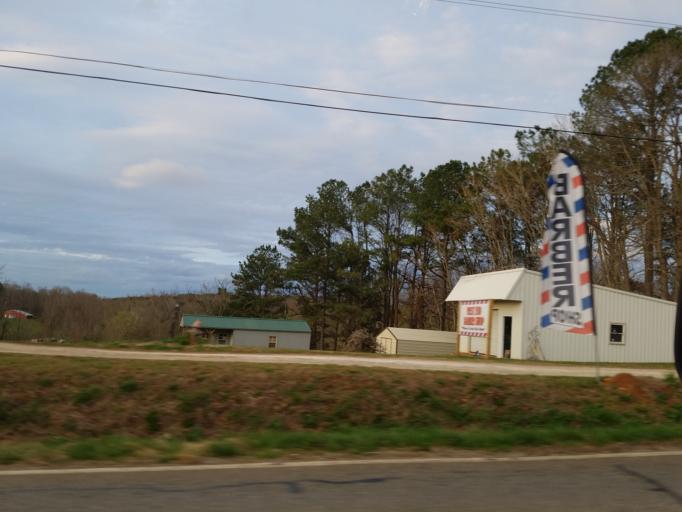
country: US
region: Georgia
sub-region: Pickens County
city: Jasper
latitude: 34.4683
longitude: -84.4927
